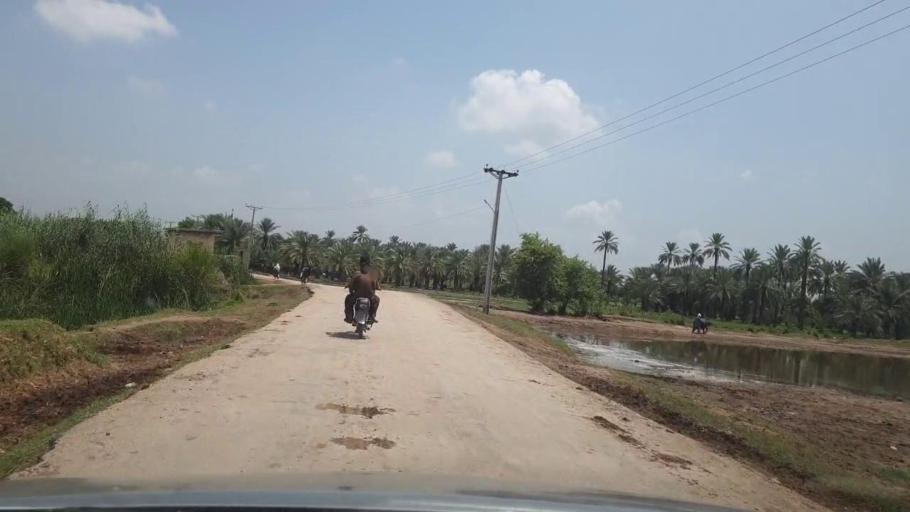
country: PK
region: Sindh
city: Pir jo Goth
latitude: 27.6005
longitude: 68.6032
